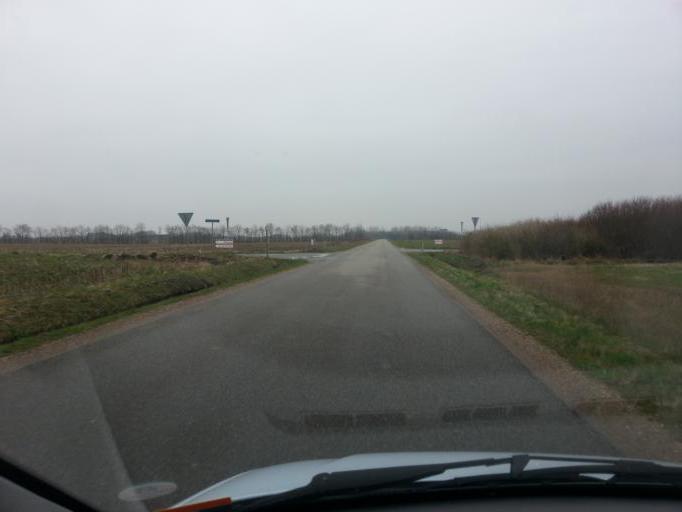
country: DK
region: South Denmark
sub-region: Esbjerg Kommune
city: Bramming
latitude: 55.5539
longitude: 8.7162
